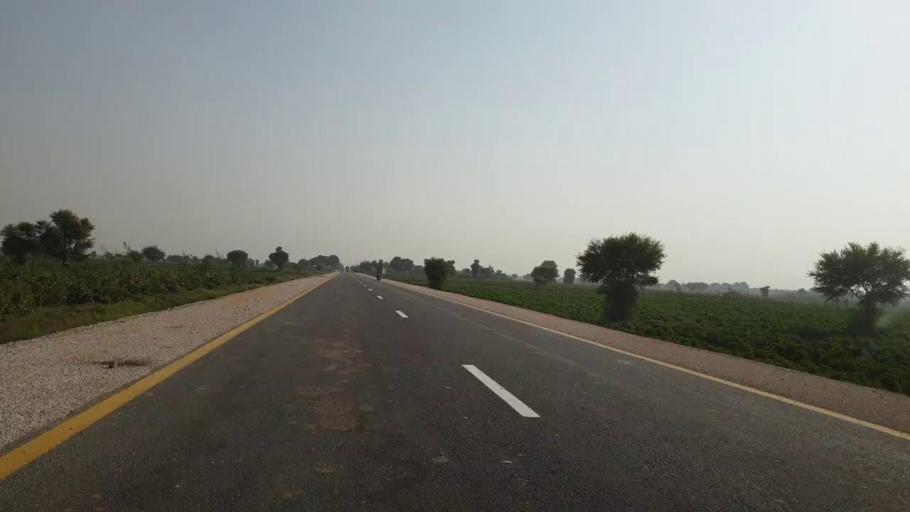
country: PK
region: Sindh
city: Bhan
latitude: 26.5404
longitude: 67.7876
